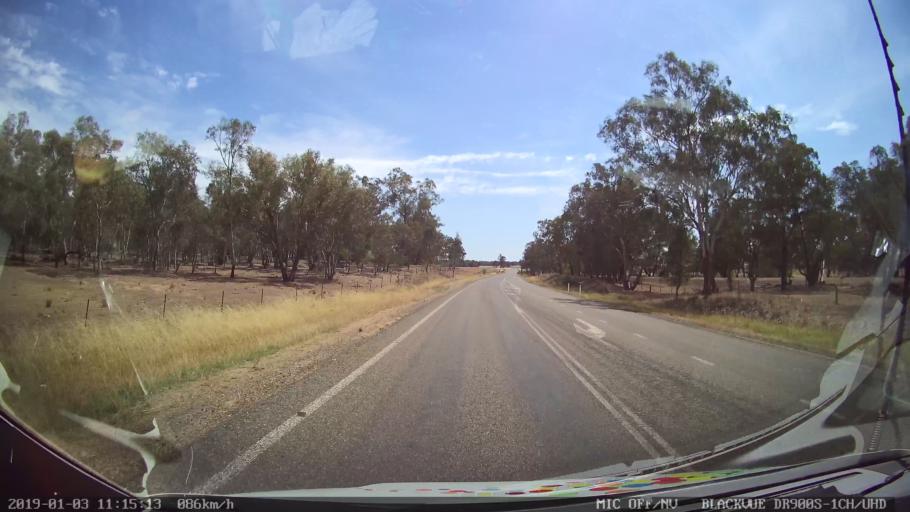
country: AU
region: New South Wales
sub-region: Young
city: Young
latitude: -34.1664
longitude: 148.2628
